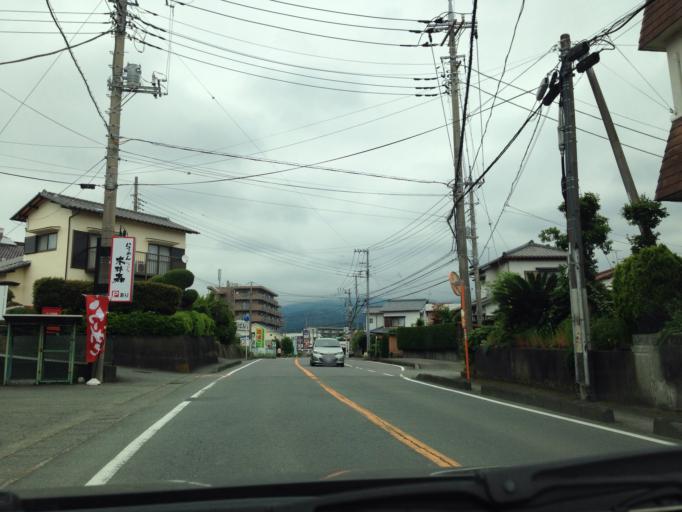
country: JP
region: Shizuoka
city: Mishima
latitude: 35.1648
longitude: 138.9112
